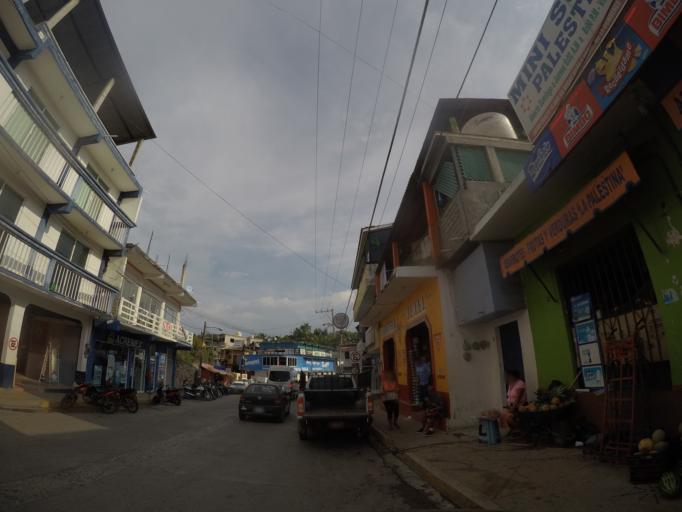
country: MX
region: Oaxaca
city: San Pedro Pochutla
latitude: 15.7476
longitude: -96.4668
